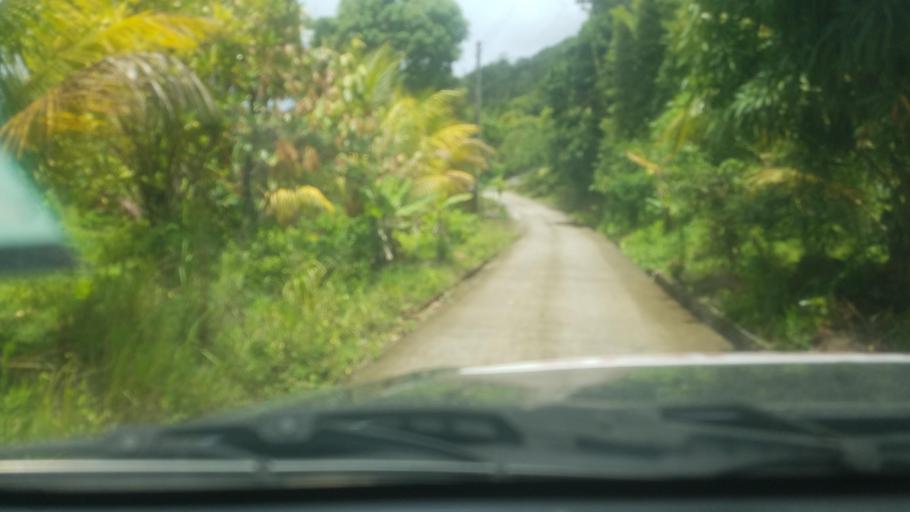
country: LC
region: Laborie Quarter
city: Laborie
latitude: 13.7754
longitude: -60.9969
